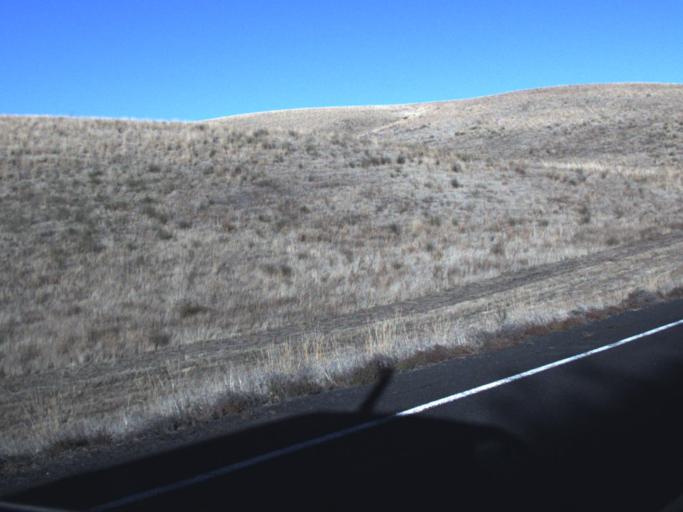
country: US
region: Washington
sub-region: Adams County
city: Ritzville
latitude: 46.6777
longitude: -118.3496
